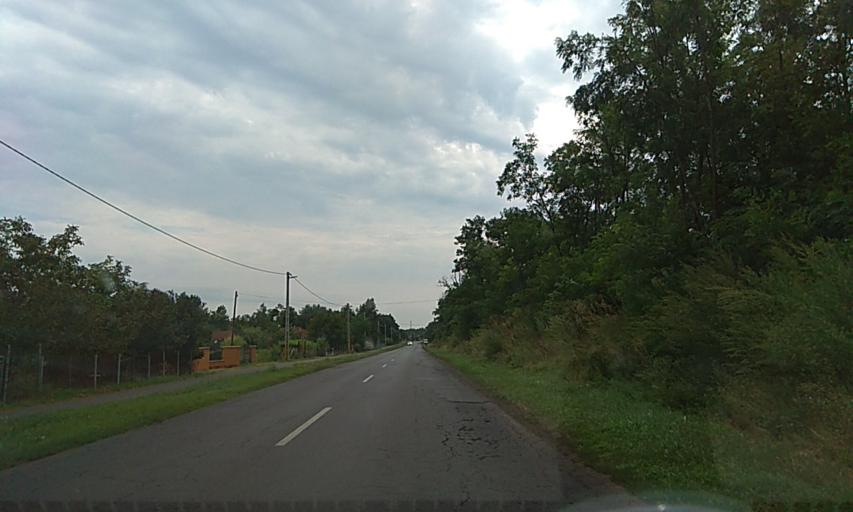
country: HU
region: Szabolcs-Szatmar-Bereg
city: Nyiregyhaza
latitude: 47.9956
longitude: 21.7027
